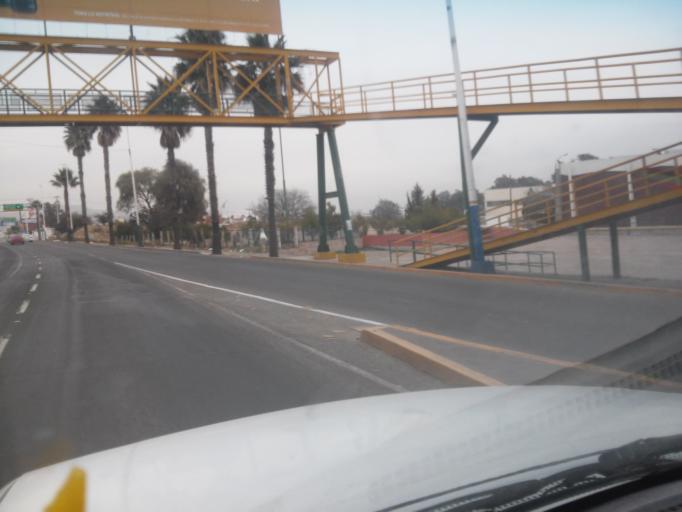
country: MX
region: Durango
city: Victoria de Durango
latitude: 24.0311
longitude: -104.6856
